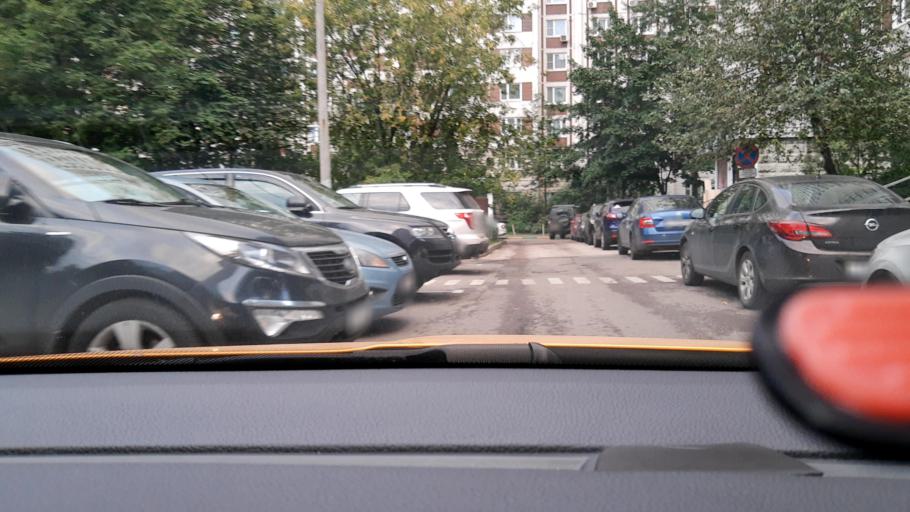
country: RU
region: Moskovskaya
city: Krasnogorsk
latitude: 55.8532
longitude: 37.3452
